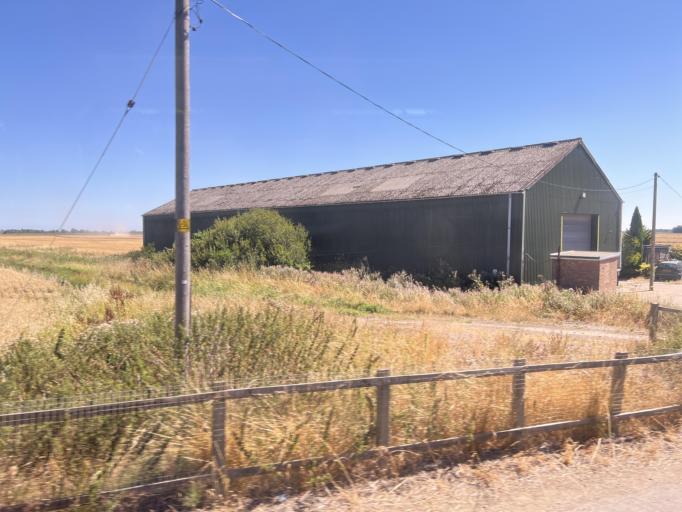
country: GB
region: England
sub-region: Lincolnshire
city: Spilsby
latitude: 53.0830
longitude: 0.0884
